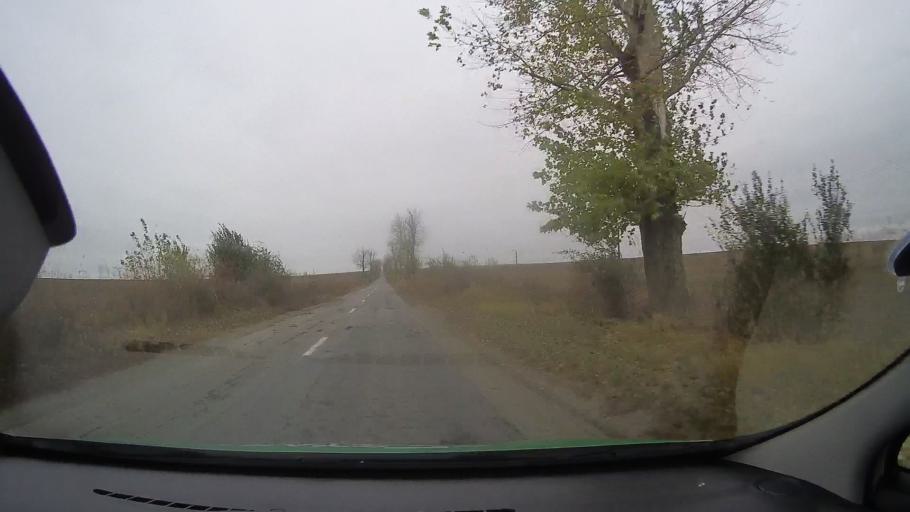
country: RO
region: Constanta
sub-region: Comuna Pantelimon
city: Pantelimon
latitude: 44.5546
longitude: 28.3259
